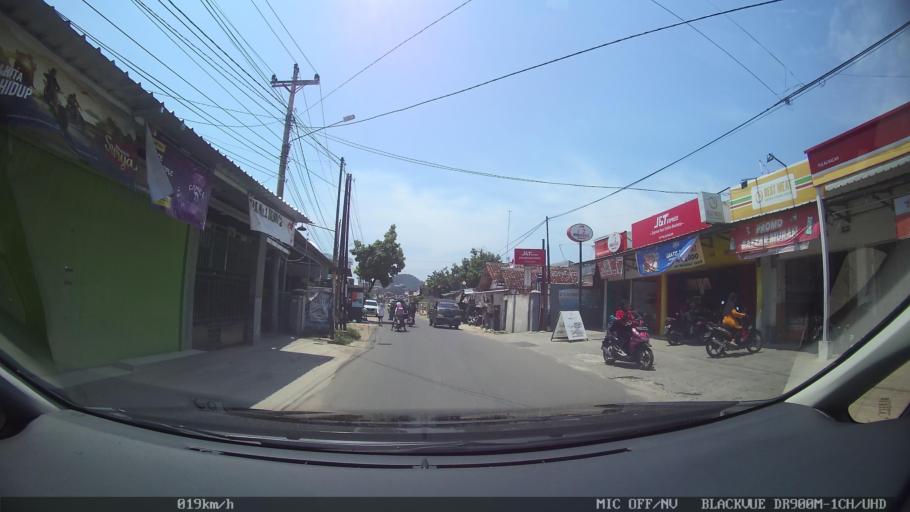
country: ID
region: Lampung
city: Bandarlampung
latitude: -5.4072
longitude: 105.2695
